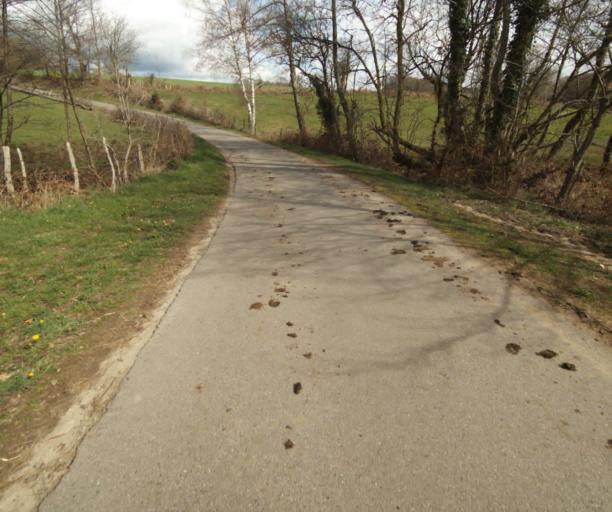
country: FR
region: Limousin
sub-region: Departement de la Correze
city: Correze
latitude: 45.3633
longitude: 1.8987
